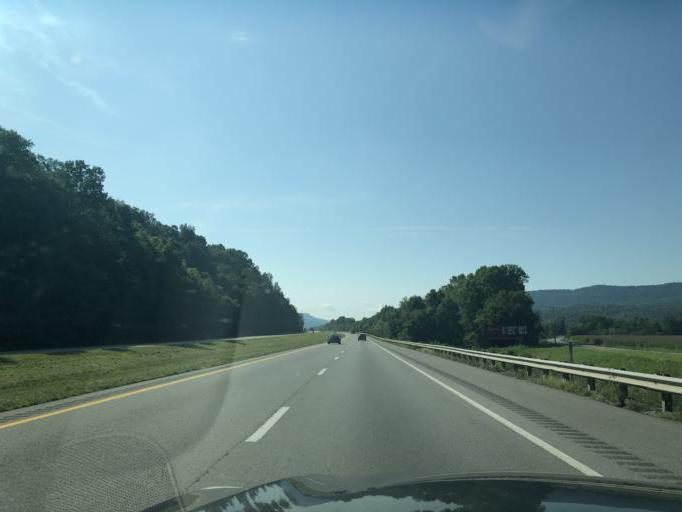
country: US
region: Tennessee
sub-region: Marion County
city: Monteagle
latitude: 35.1414
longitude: -85.7721
